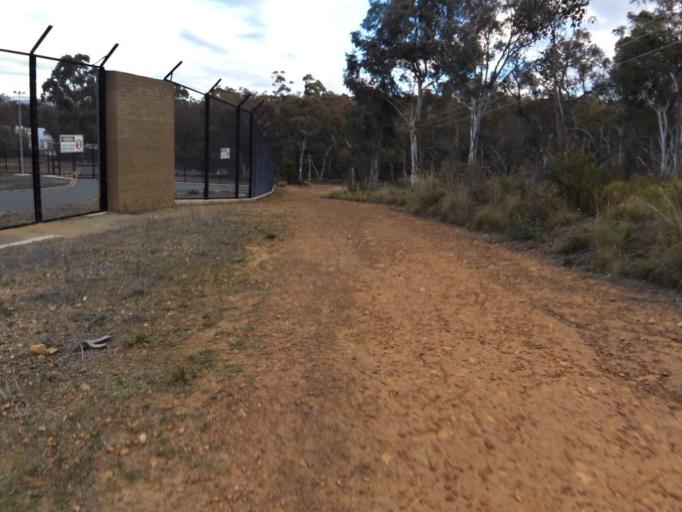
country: AU
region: Australian Capital Territory
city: Acton
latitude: -35.2694
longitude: 149.1082
